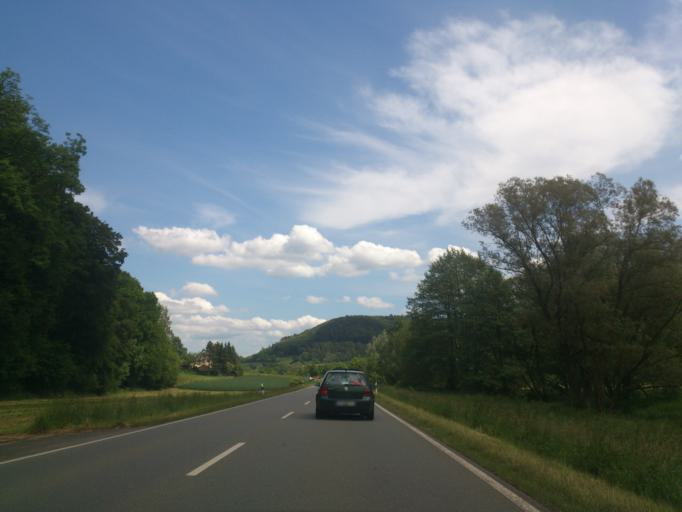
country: DE
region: North Rhine-Westphalia
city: Beverungen
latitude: 51.6512
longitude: 9.3304
